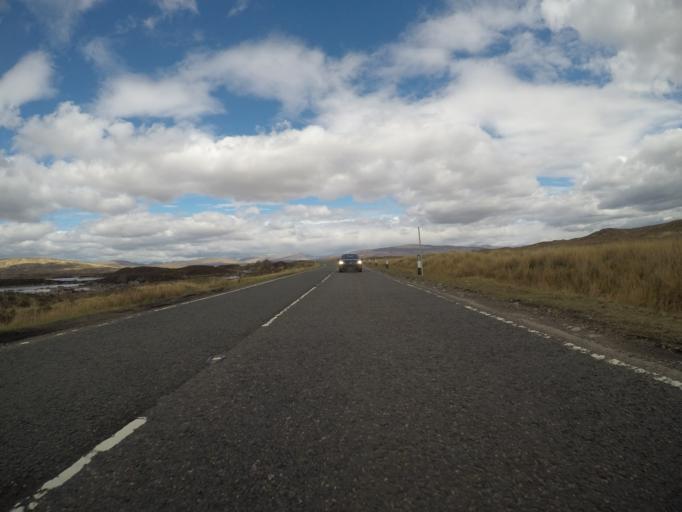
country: GB
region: Scotland
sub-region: Highland
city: Spean Bridge
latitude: 56.5946
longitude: -4.7437
